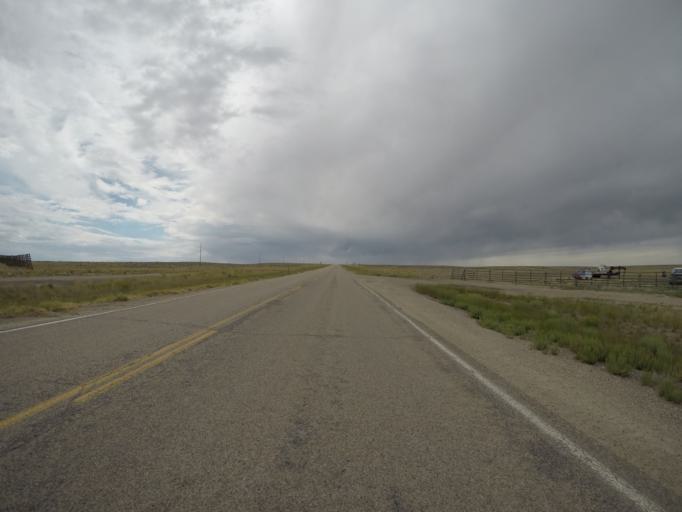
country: US
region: Wyoming
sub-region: Lincoln County
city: Kemmerer
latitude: 41.9801
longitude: -110.0624
